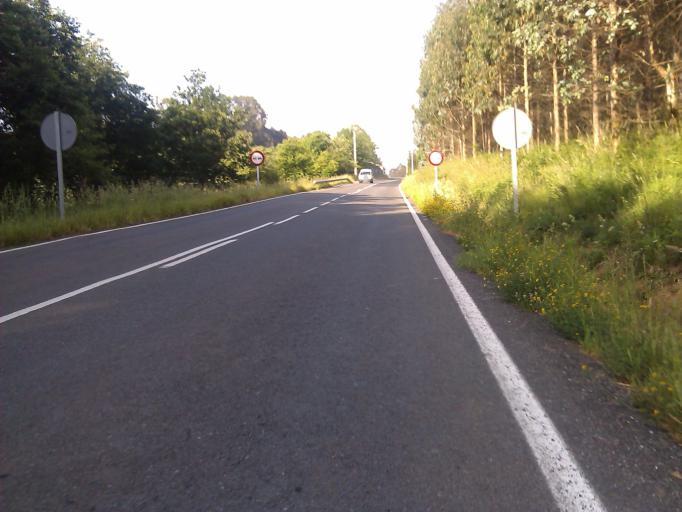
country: ES
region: Galicia
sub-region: Provincia da Coruna
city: Santiso
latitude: 42.9068
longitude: -8.0556
